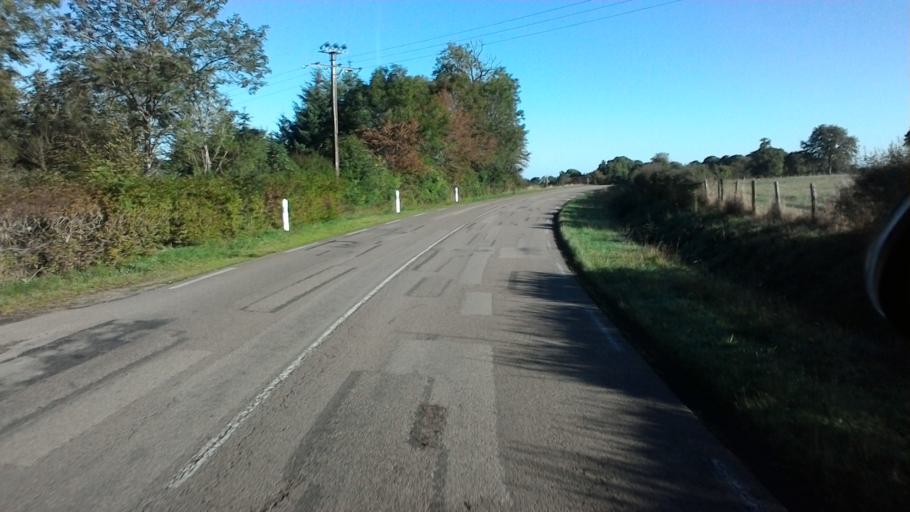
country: FR
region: Bourgogne
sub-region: Departement de la Cote-d'Or
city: Saulieu
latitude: 47.3321
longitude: 4.2700
